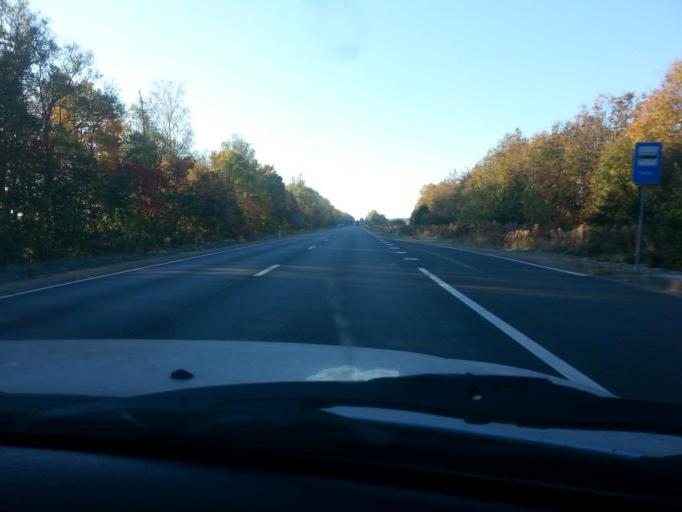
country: LV
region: Jelgava
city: Jelgava
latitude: 56.5197
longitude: 23.7036
